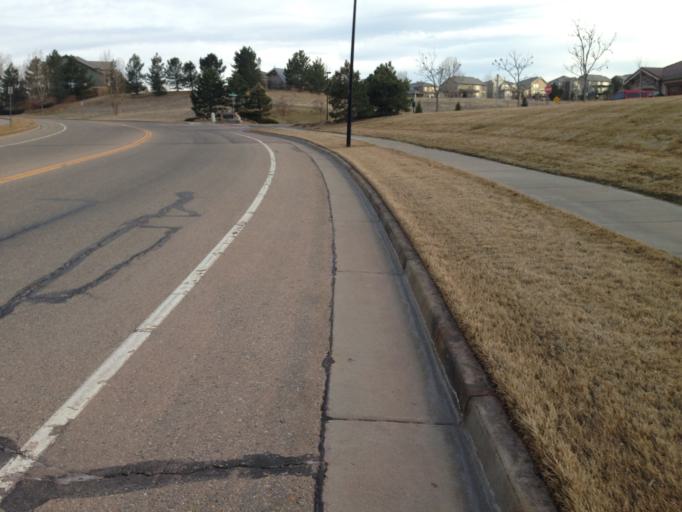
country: US
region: Colorado
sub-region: Boulder County
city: Superior
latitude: 39.9270
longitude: -105.1611
